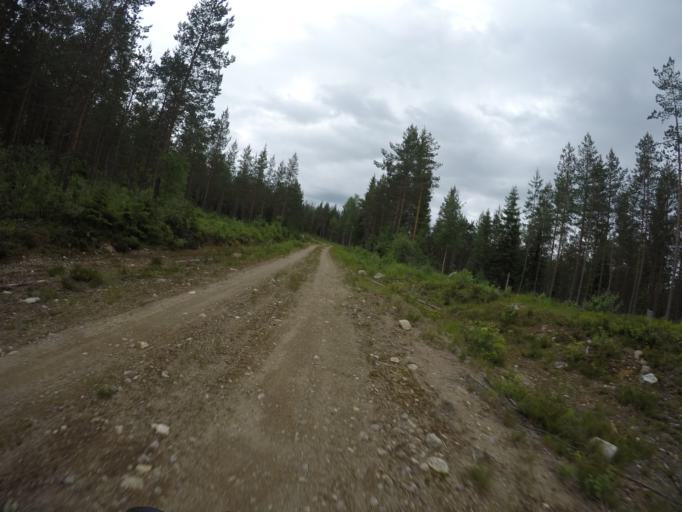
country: SE
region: Dalarna
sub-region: Ludvika Kommun
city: Abborrberget
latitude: 60.0632
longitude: 14.5601
